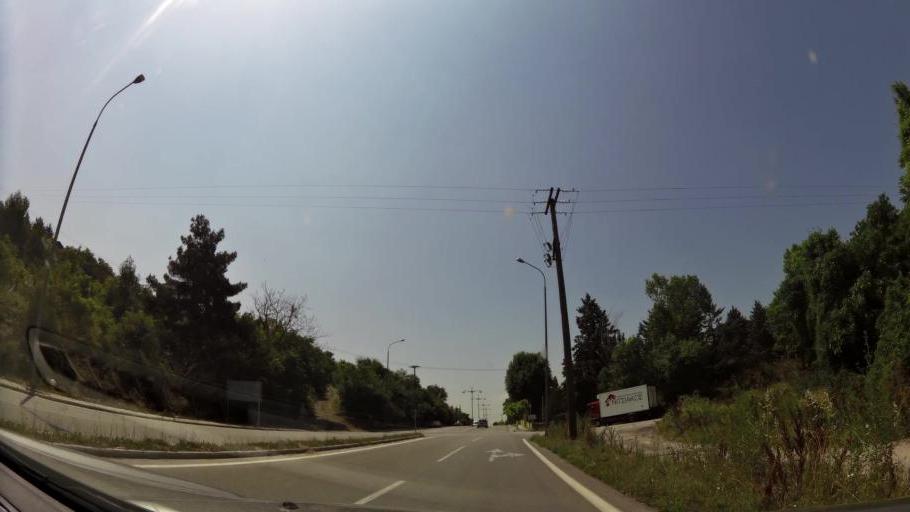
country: GR
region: West Macedonia
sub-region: Nomos Kozanis
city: Kozani
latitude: 40.3121
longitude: 21.7841
